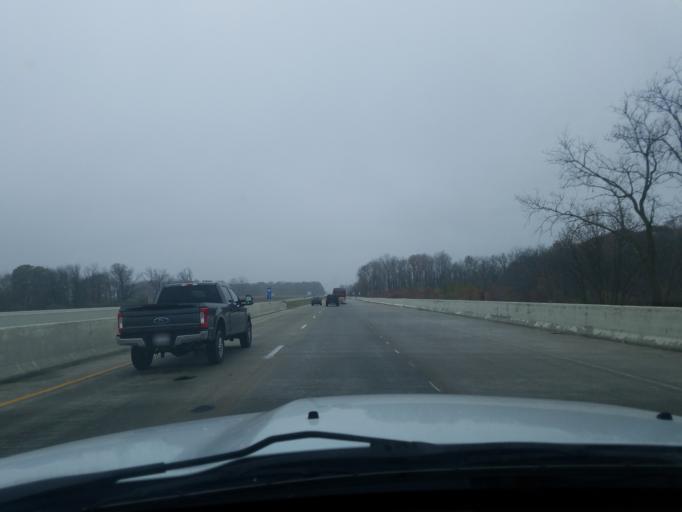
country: US
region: Indiana
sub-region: Hamilton County
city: Westfield
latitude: 40.0941
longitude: -86.1278
